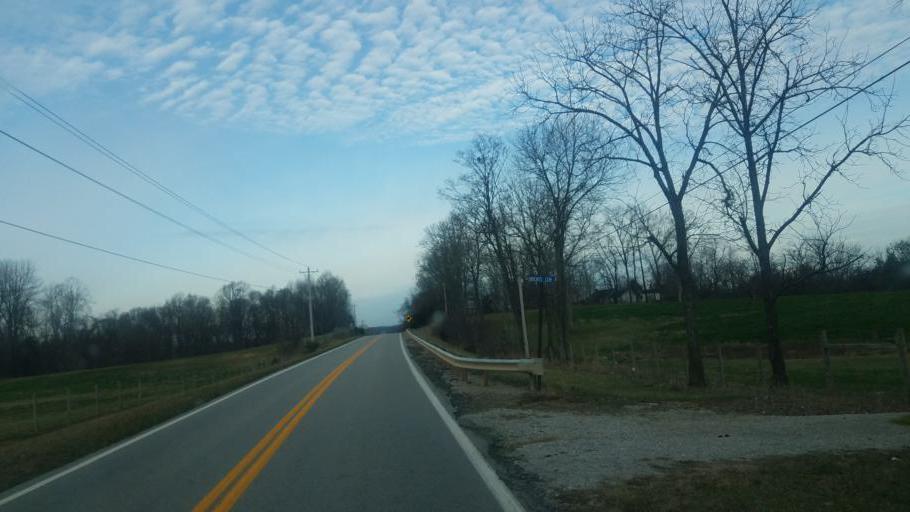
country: US
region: Kentucky
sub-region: Clinton County
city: Albany
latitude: 36.7610
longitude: -85.1600
